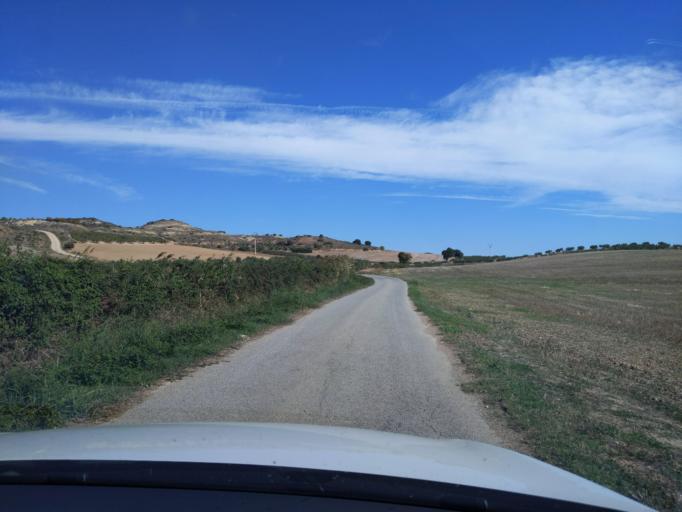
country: ES
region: Navarre
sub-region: Provincia de Navarra
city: Arroniz
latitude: 42.5674
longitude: -2.0601
